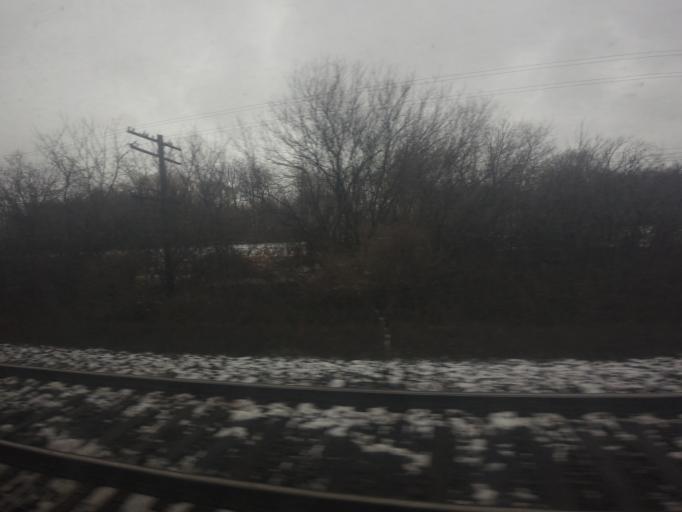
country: CA
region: Ontario
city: Quinte West
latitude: 44.0801
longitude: -77.6464
